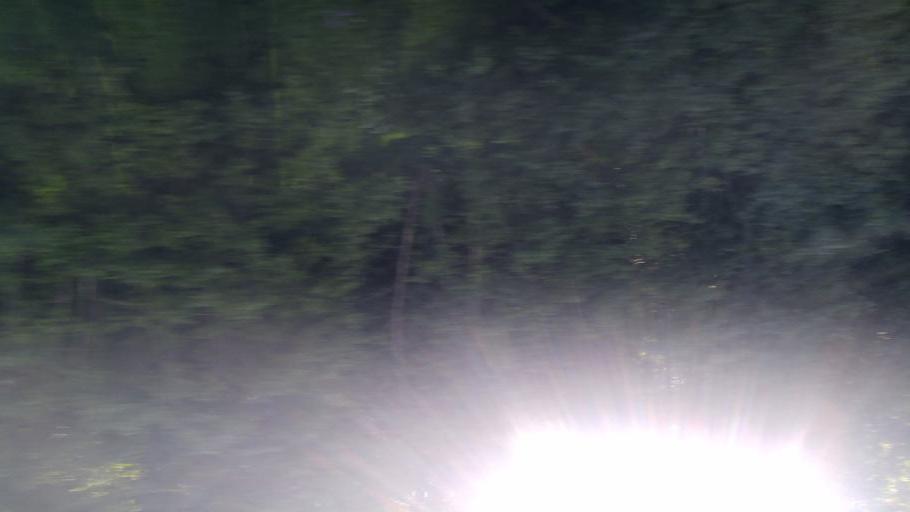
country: NO
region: Sor-Trondelag
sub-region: Trondheim
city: Trondheim
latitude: 63.3667
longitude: 10.3643
